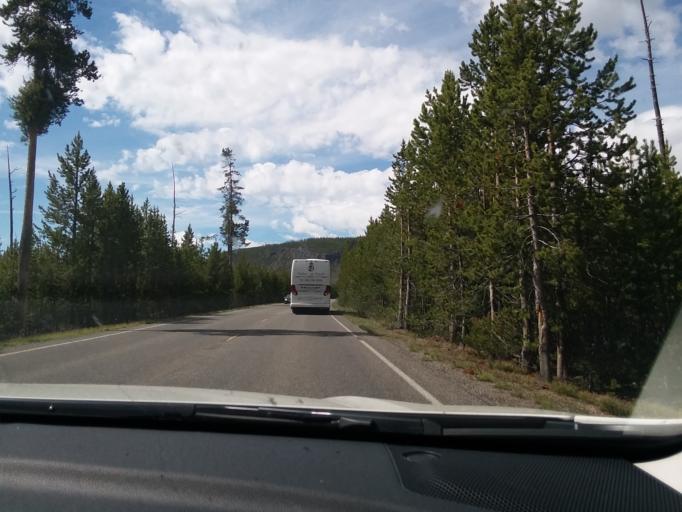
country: US
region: Montana
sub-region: Gallatin County
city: West Yellowstone
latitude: 44.4770
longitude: -110.8551
